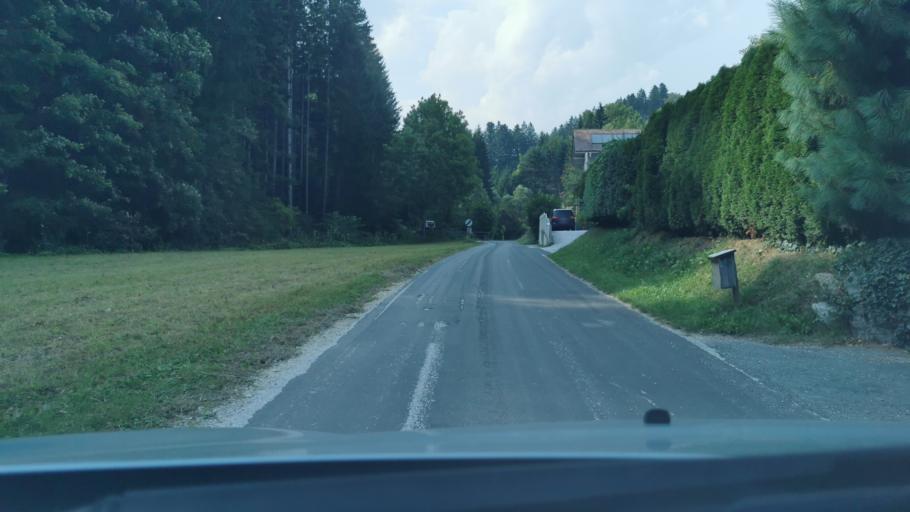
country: AT
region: Styria
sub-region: Politischer Bezirk Weiz
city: Fischbach
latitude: 47.3960
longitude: 15.6553
